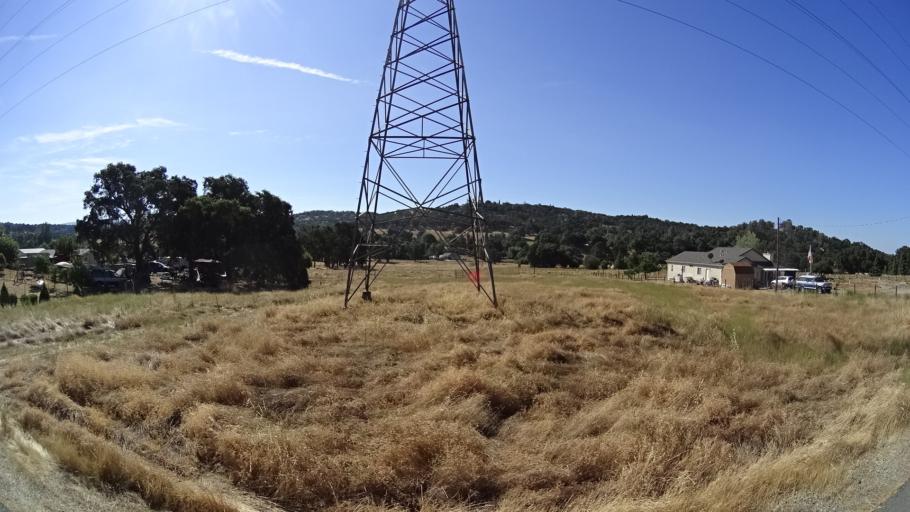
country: US
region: California
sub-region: Calaveras County
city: Rancho Calaveras
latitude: 38.1576
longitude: -120.8549
